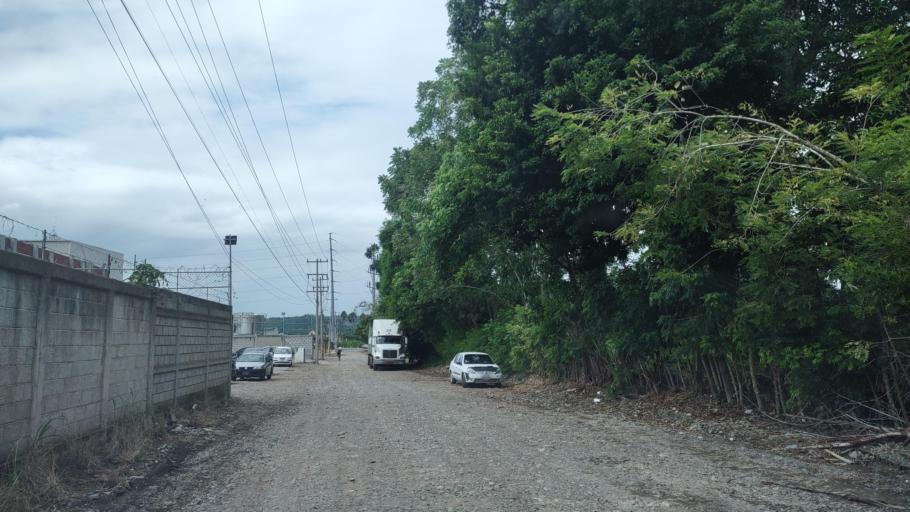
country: MX
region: Veracruz
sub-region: Papantla
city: Residencial Tajin
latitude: 20.5933
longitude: -97.4196
